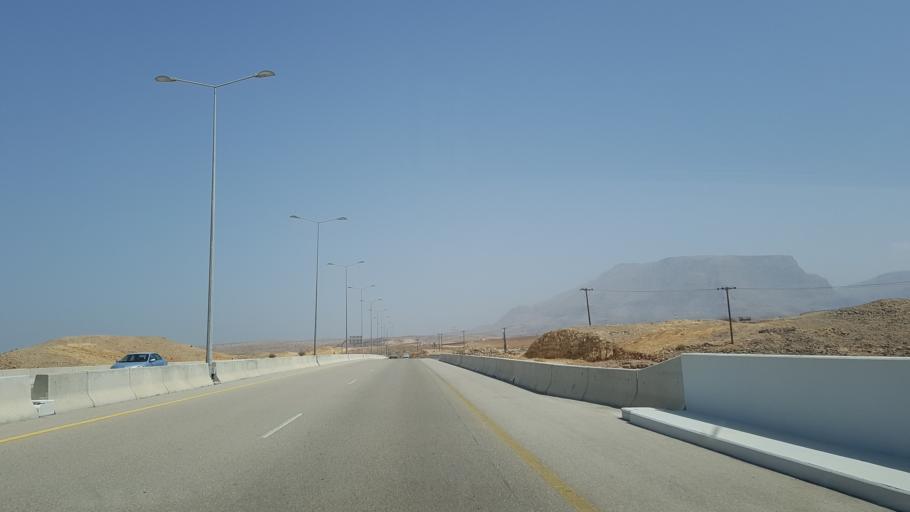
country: OM
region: Ash Sharqiyah
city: Al Qabil
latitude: 23.1082
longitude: 58.9827
